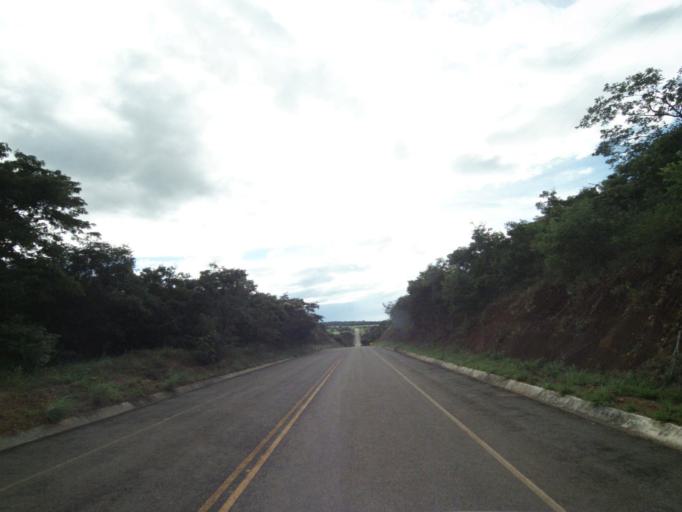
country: BR
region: Goias
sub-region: Jaragua
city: Jaragua
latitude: -15.8427
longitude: -49.3392
